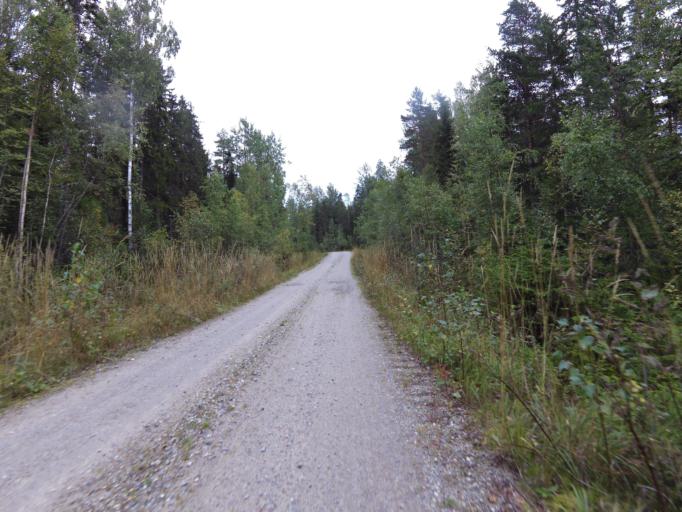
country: SE
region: Gaevleborg
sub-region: Gavle Kommun
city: Valbo
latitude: 60.7408
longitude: 17.0237
